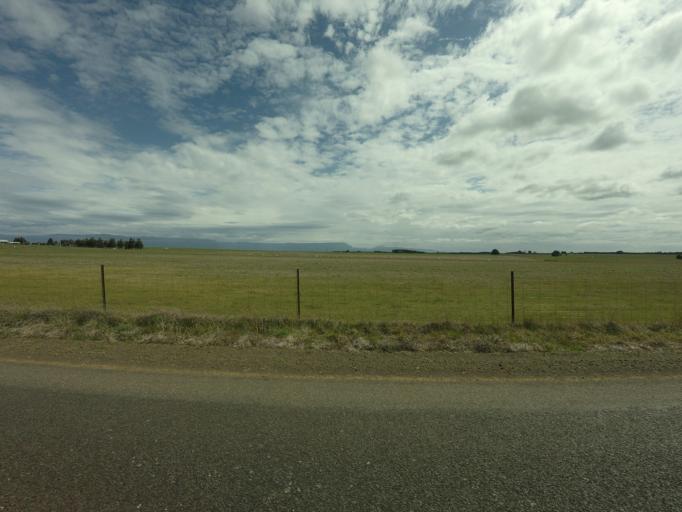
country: AU
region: Tasmania
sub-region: Northern Midlands
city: Longford
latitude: -41.7006
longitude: 147.1964
